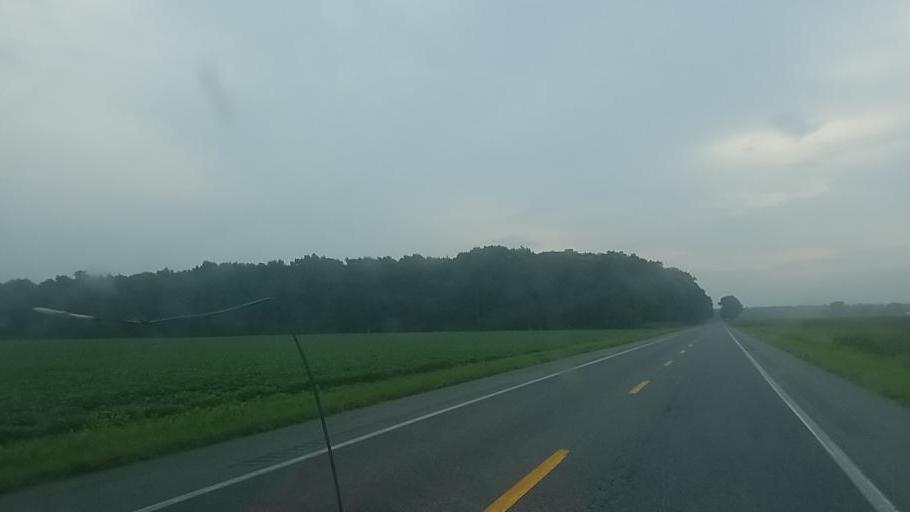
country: US
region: Maryland
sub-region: Wicomico County
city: Pittsville
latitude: 38.4522
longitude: -75.4041
